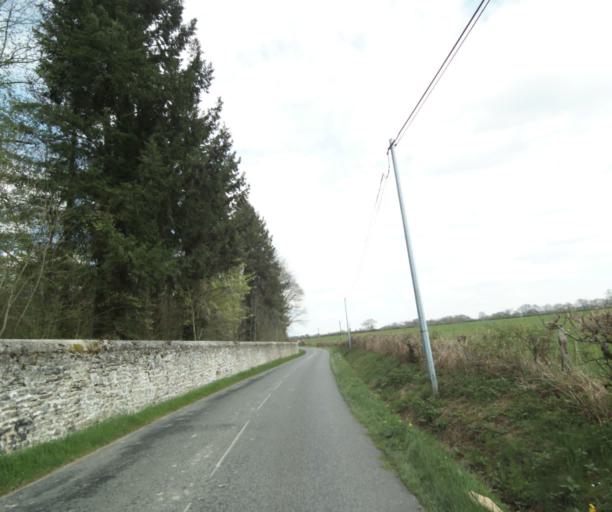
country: FR
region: Bourgogne
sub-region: Departement de Saone-et-Loire
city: Palinges
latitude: 46.5355
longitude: 4.2133
